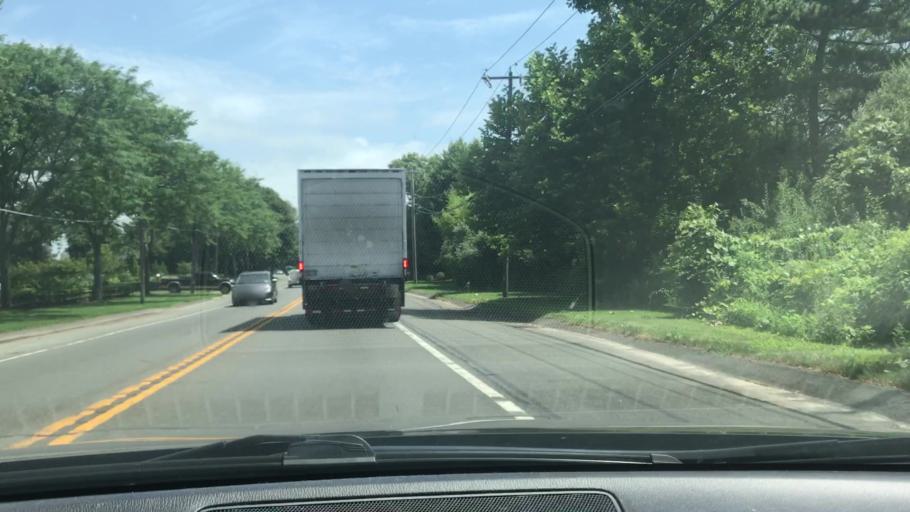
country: US
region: New York
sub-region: Suffolk County
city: Water Mill
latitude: 40.9209
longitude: -72.3403
